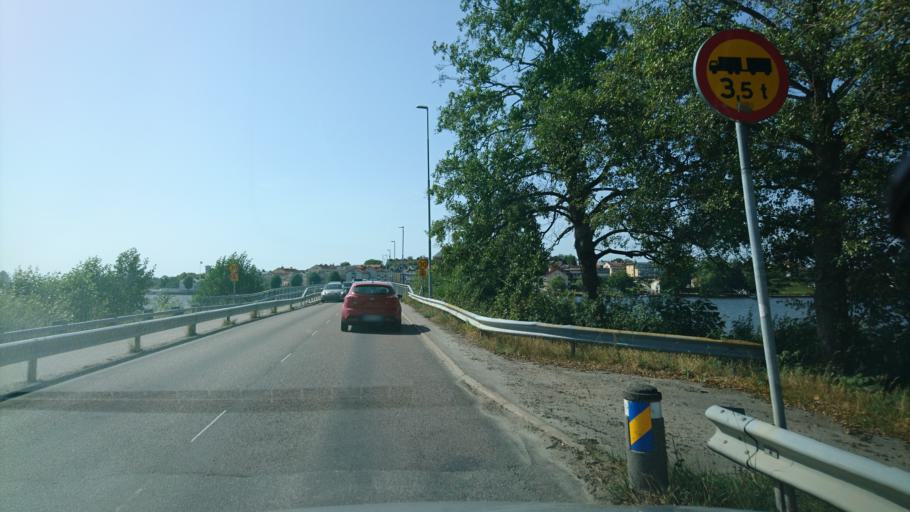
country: SE
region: Soedermanland
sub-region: Strangnas Kommun
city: Strangnas
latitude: 59.3804
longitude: 17.0392
